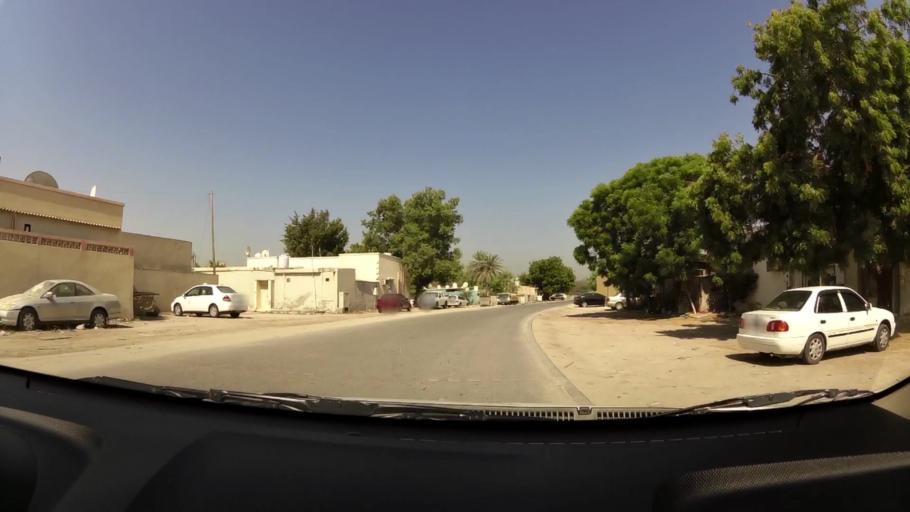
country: AE
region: Umm al Qaywayn
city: Umm al Qaywayn
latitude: 25.5879
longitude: 55.5756
